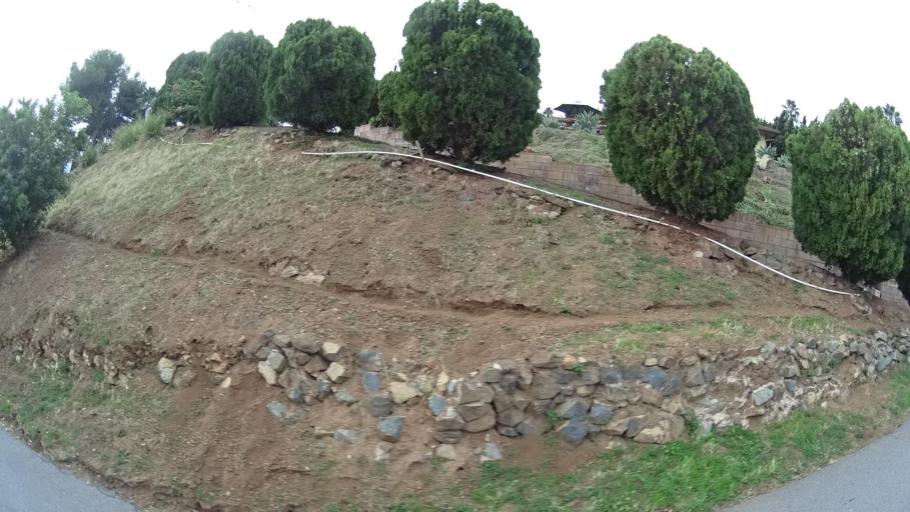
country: US
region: California
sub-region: San Diego County
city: Spring Valley
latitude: 32.7458
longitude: -117.0077
